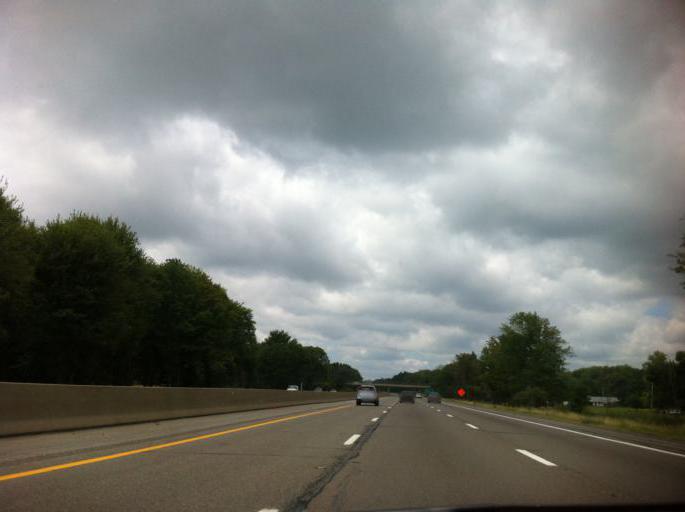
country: US
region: Ohio
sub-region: Lorain County
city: North Ridgeville
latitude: 41.3797
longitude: -82.0133
